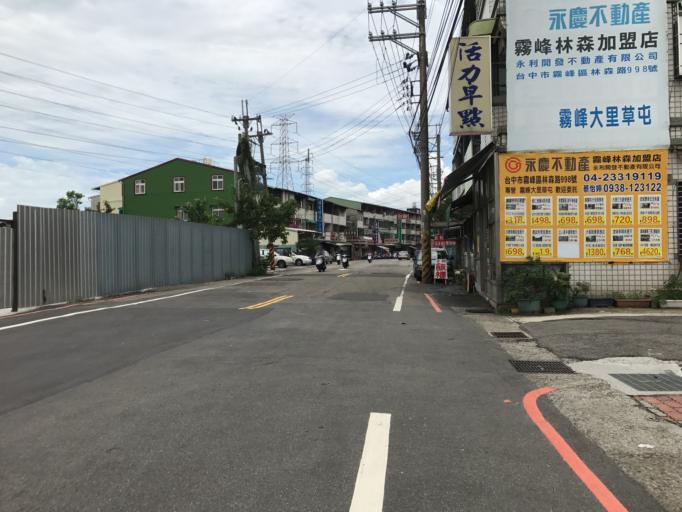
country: TW
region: Taiwan
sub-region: Taichung City
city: Taichung
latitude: 24.0844
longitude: 120.7087
